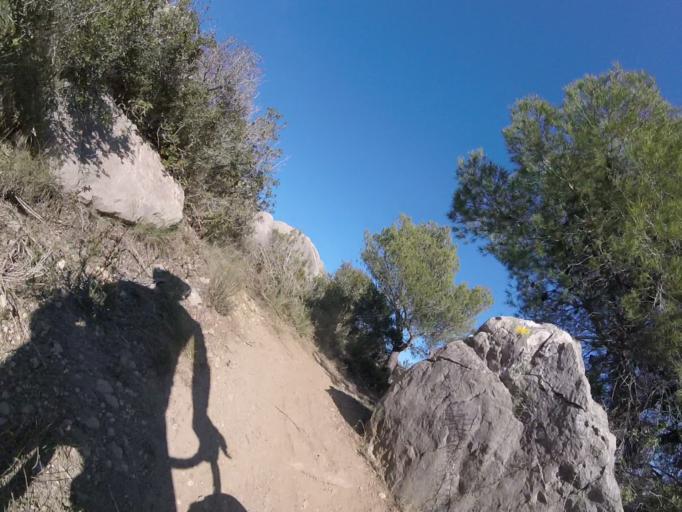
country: ES
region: Valencia
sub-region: Provincia de Castello
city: Orpesa/Oropesa del Mar
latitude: 40.1078
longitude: 0.1181
